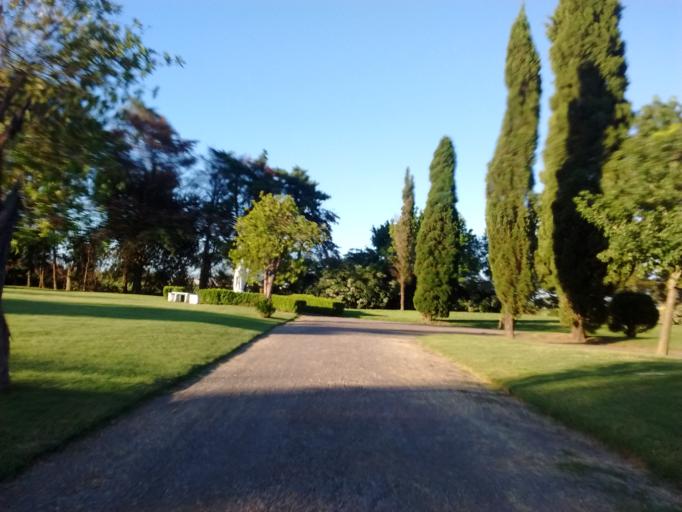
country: AR
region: Santa Fe
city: Funes
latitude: -32.9183
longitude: -60.7913
